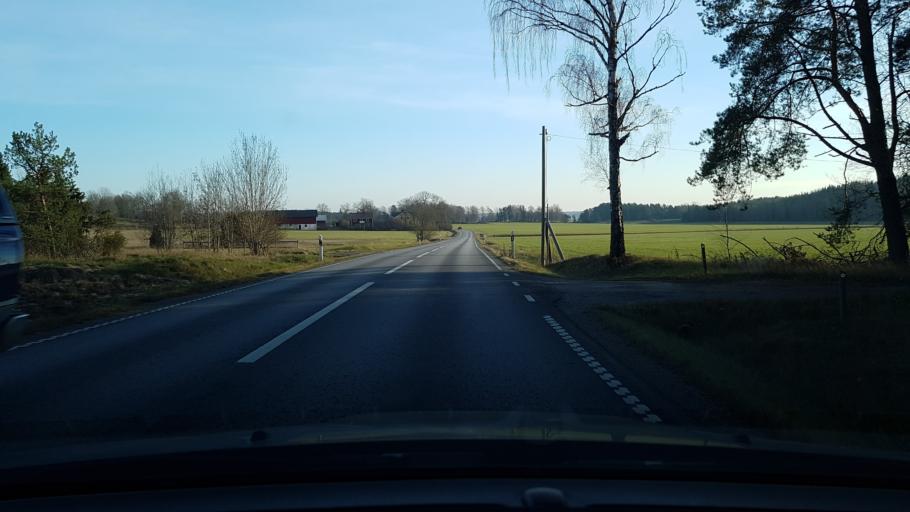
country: SE
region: Stockholm
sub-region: Norrtalje Kommun
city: Nykvarn
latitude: 59.7437
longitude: 18.1269
